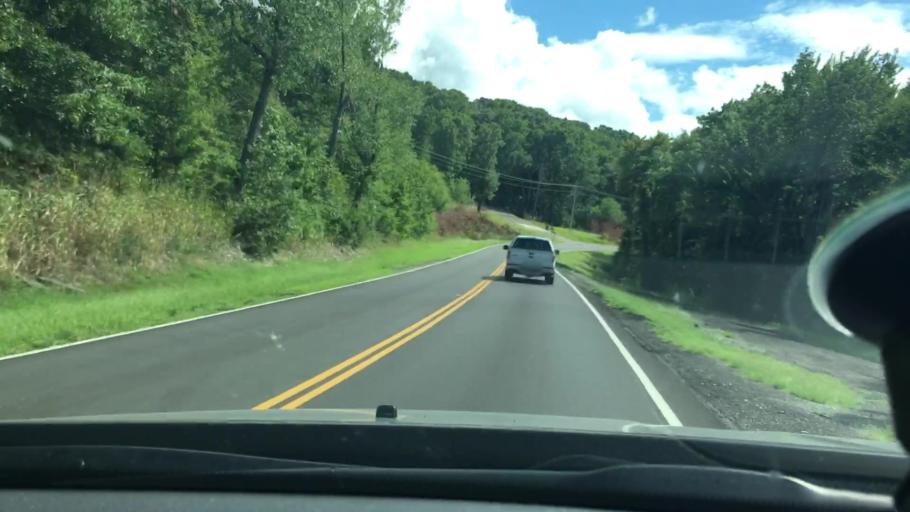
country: US
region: Oklahoma
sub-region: Sequoyah County
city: Vian
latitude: 35.6575
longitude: -94.9517
